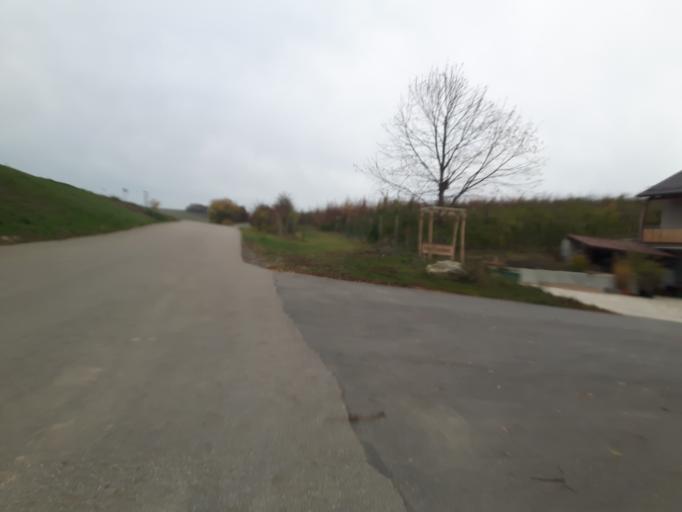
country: DE
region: Baden-Wuerttemberg
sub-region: Regierungsbezirk Stuttgart
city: Schwaigern
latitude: 49.1472
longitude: 9.0427
